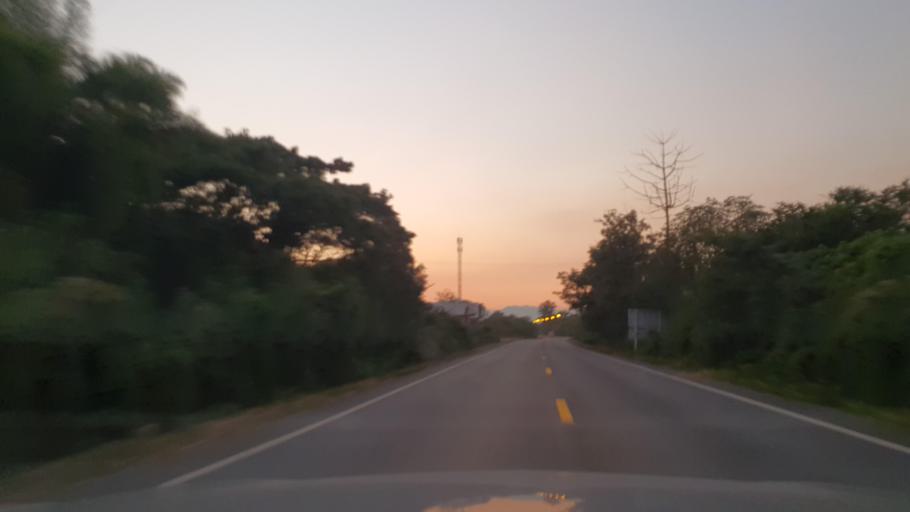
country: TH
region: Phayao
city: Dok Kham Tai
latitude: 19.1477
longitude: 100.0053
